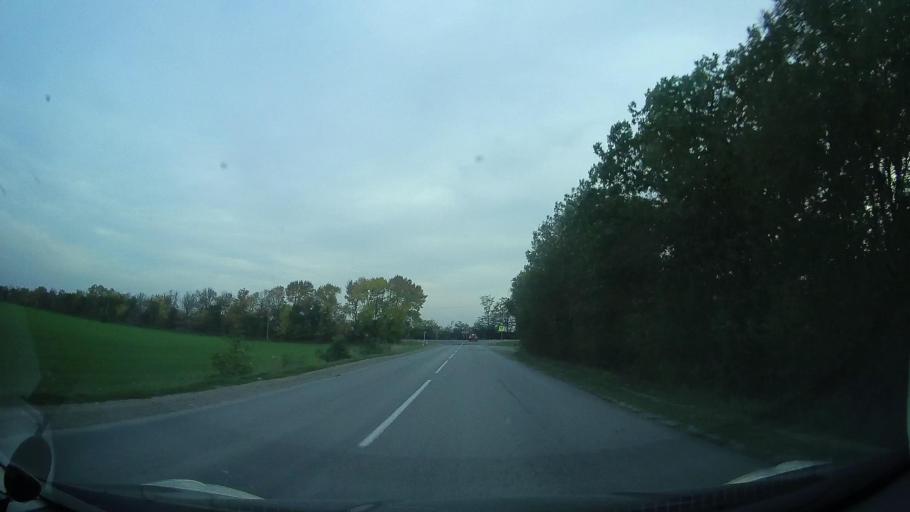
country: RU
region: Rostov
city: Kirovskaya
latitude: 47.0028
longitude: 39.9789
